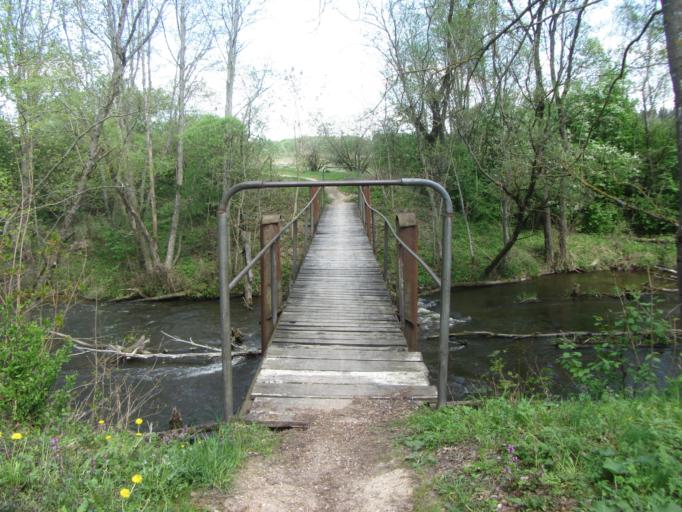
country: LT
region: Utenos apskritis
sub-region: Anyksciai
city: Anyksciai
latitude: 55.4271
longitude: 25.0642
